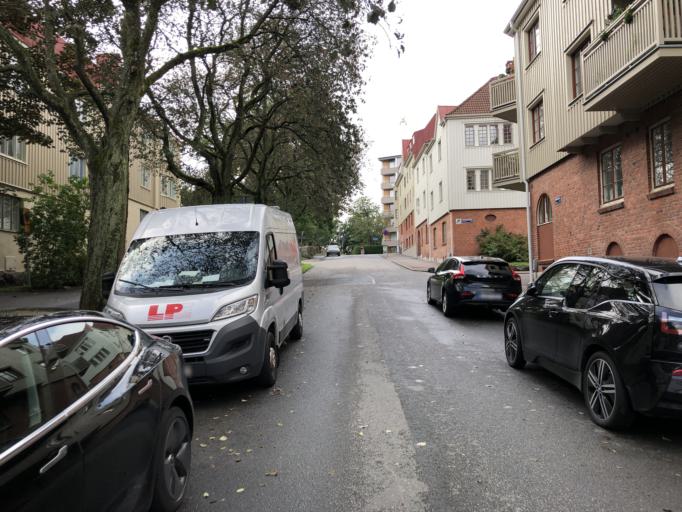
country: SE
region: Vaestra Goetaland
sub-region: Goteborg
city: Majorna
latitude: 57.6937
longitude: 11.9247
